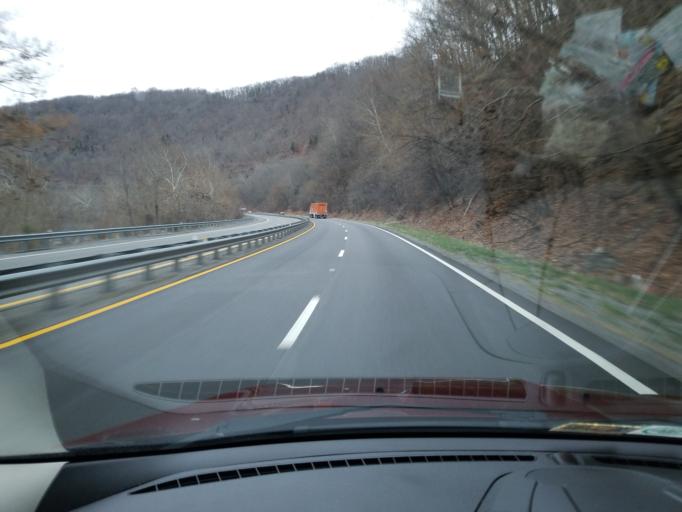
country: US
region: Virginia
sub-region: Giles County
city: Narrows
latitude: 37.3878
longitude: -80.8295
